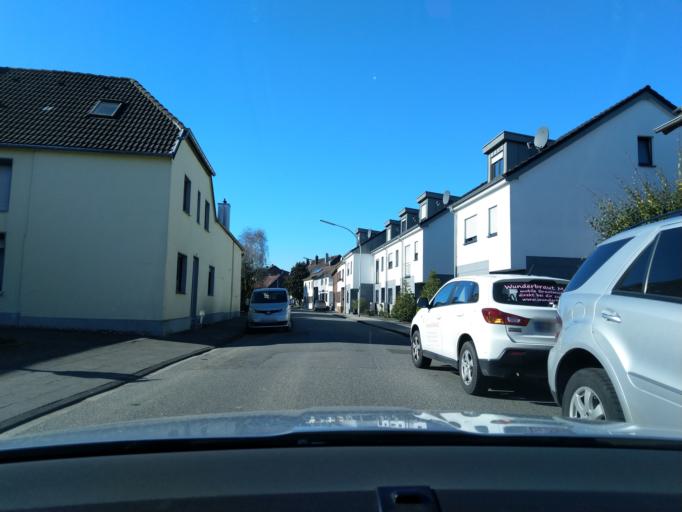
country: DE
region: North Rhine-Westphalia
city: Erkelenz
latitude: 51.1112
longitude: 6.3930
